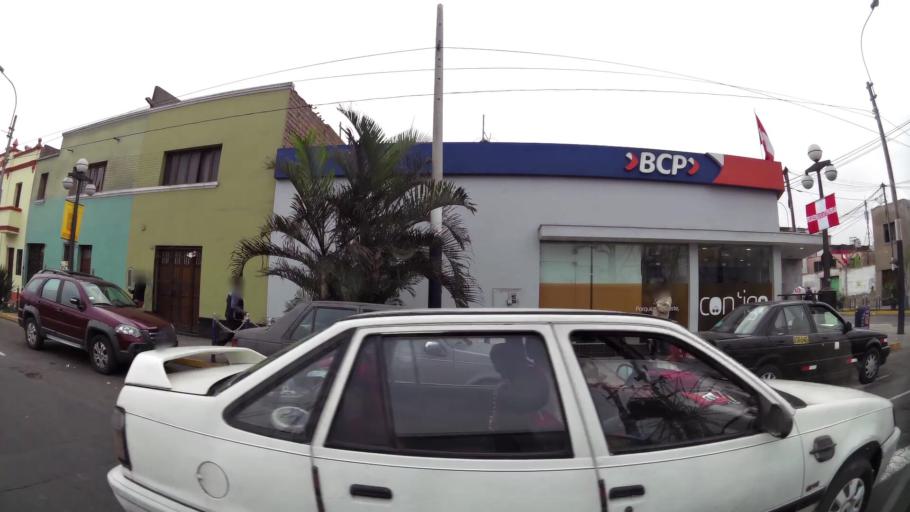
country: PE
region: Lima
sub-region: Lima
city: Surco
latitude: -12.1687
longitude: -77.0263
